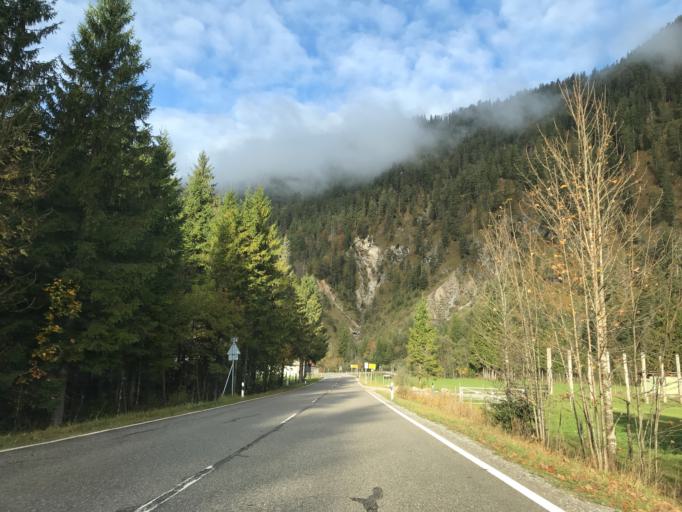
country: DE
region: Bavaria
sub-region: Upper Bavaria
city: Jachenau
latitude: 47.5588
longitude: 11.4389
